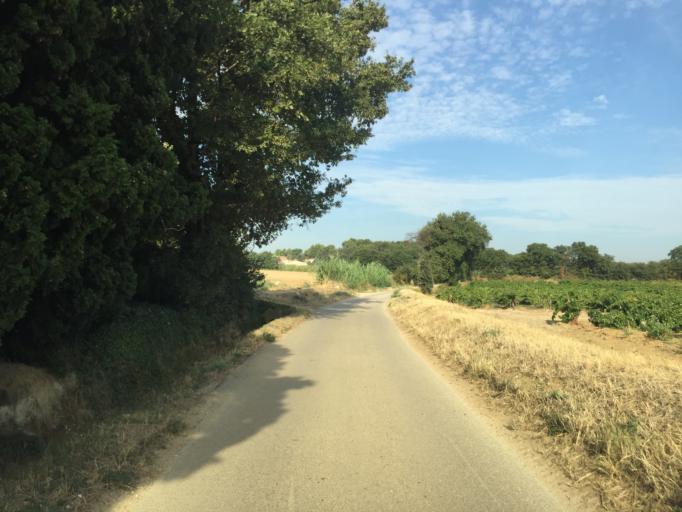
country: FR
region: Provence-Alpes-Cote d'Azur
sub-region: Departement du Vaucluse
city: Courthezon
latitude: 44.0797
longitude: 4.8632
